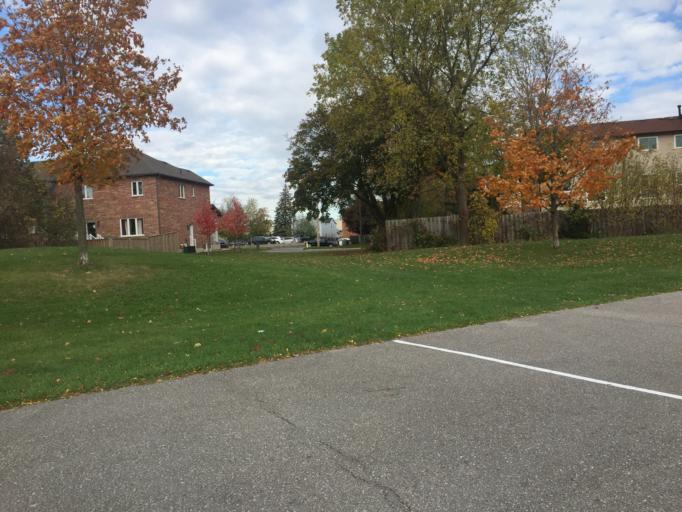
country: CA
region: Ontario
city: Oshawa
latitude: 43.9111
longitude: -78.8620
